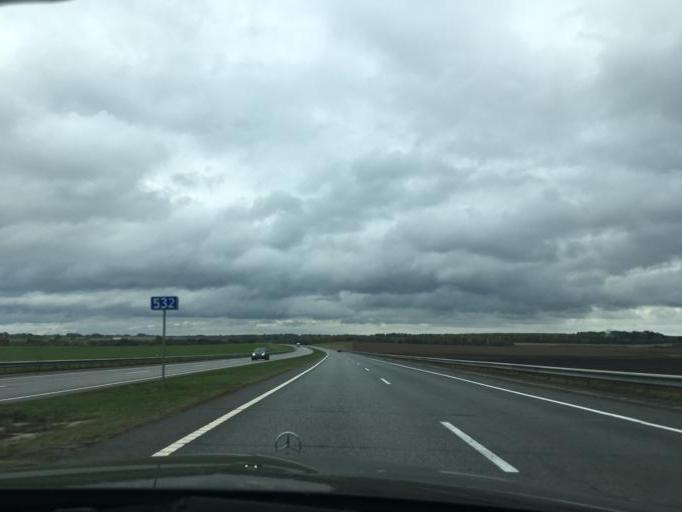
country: BY
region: Vitebsk
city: Kokhanava
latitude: 54.4739
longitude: 29.8708
